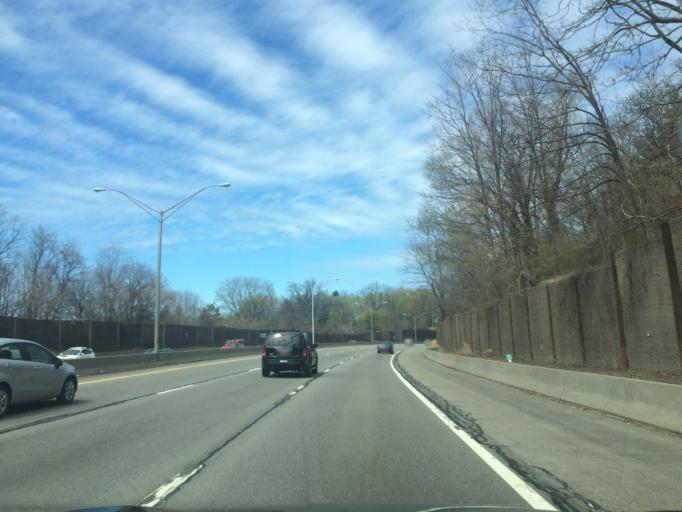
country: US
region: New York
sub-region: Monroe County
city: Pittsford
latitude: 43.1230
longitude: -77.5214
